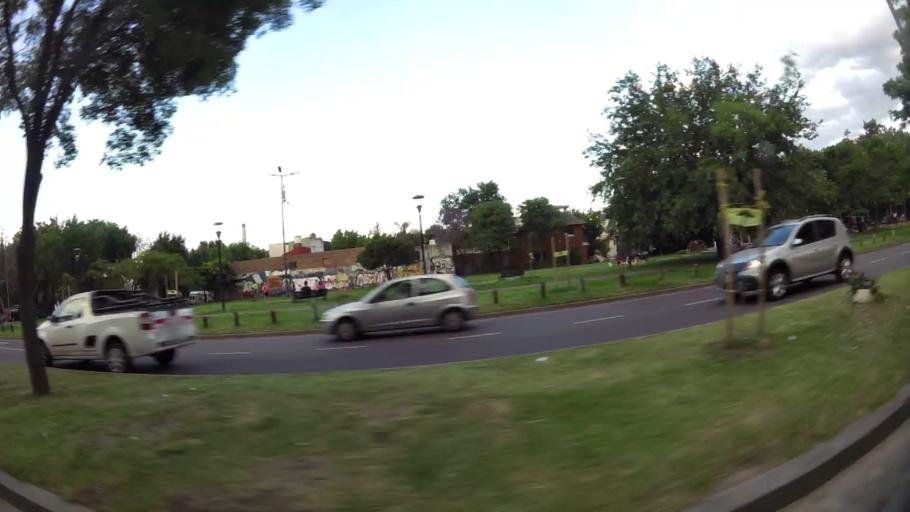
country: AR
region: Buenos Aires F.D.
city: Colegiales
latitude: -34.5618
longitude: -58.4840
